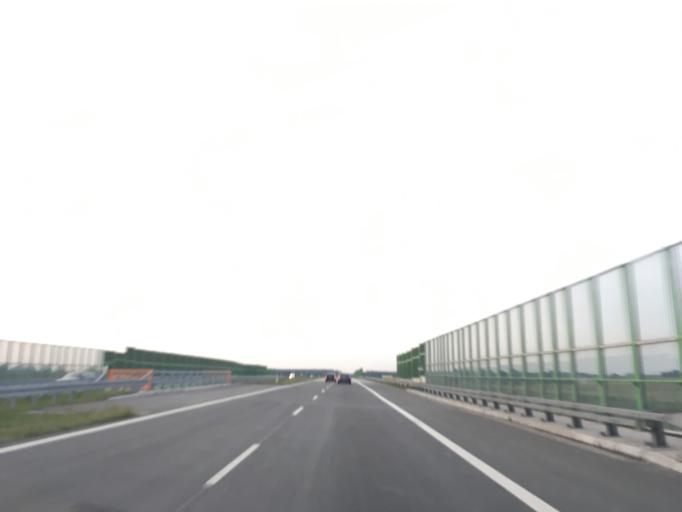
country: PL
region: Lodz Voivodeship
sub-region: Powiat lodzki wschodni
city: Tuszyn
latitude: 51.5803
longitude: 19.5932
